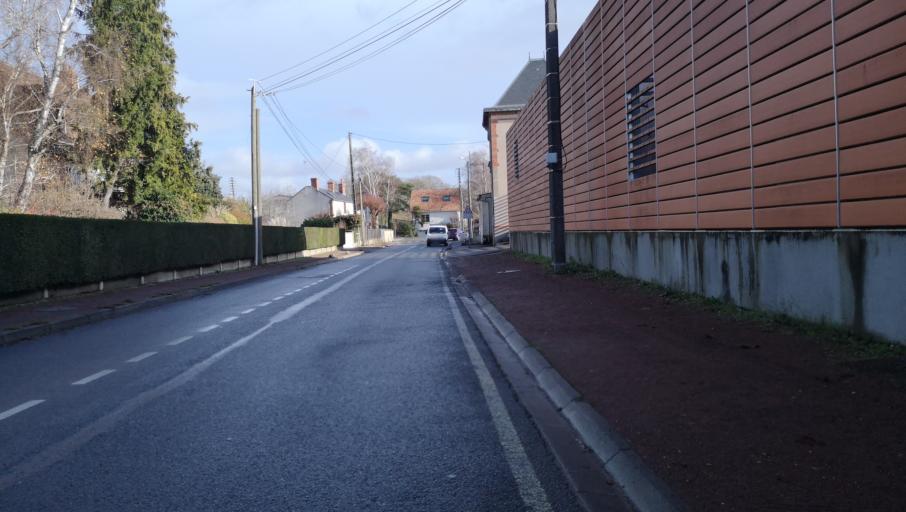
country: FR
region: Centre
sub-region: Departement du Loiret
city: Saint-Pryve-Saint-Mesmin
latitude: 47.8870
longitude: 1.8754
